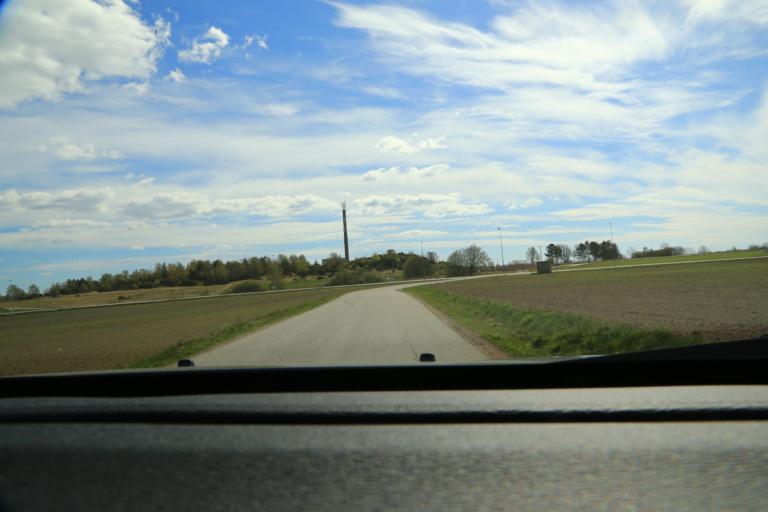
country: SE
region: Halland
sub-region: Varbergs Kommun
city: Traslovslage
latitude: 57.1106
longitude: 12.3076
